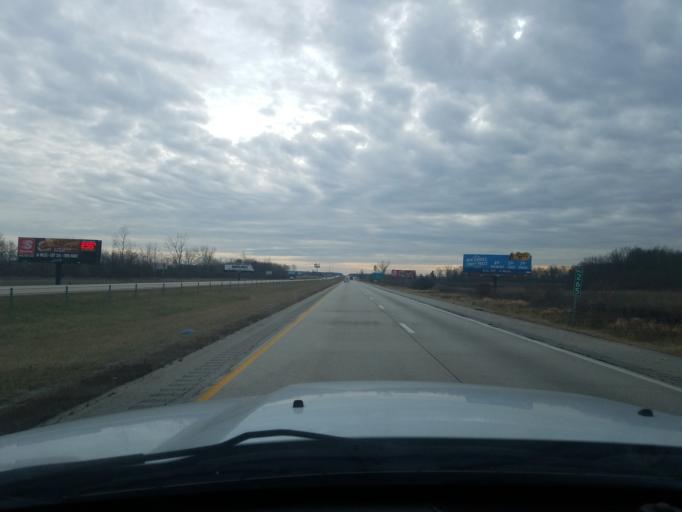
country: US
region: Indiana
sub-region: Grant County
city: Gas City
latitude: 40.5663
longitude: -85.5512
